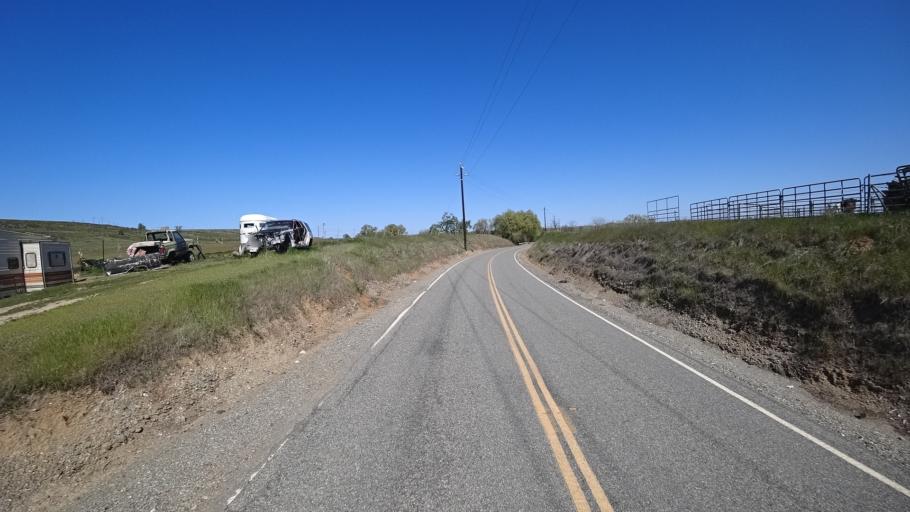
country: US
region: California
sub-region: Glenn County
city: Orland
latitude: 39.8085
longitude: -122.3304
